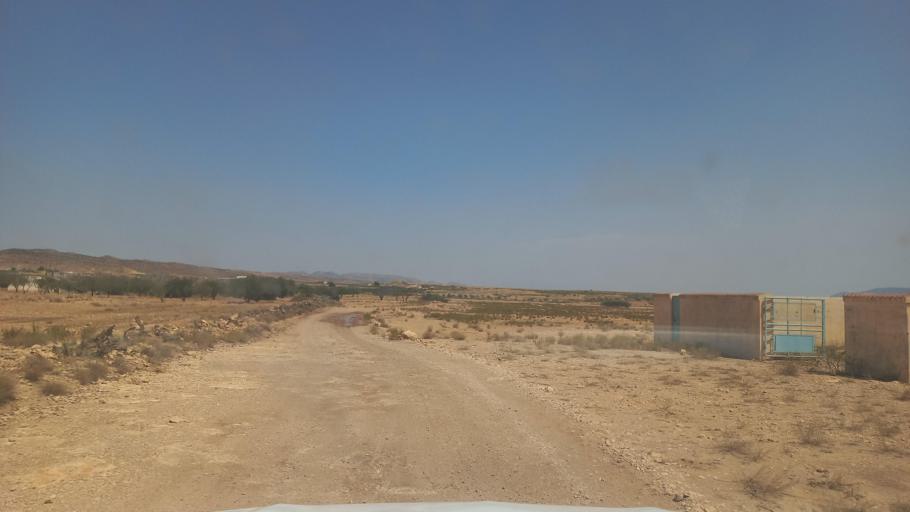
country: TN
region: Al Qasrayn
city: Kasserine
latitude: 35.2885
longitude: 8.9515
